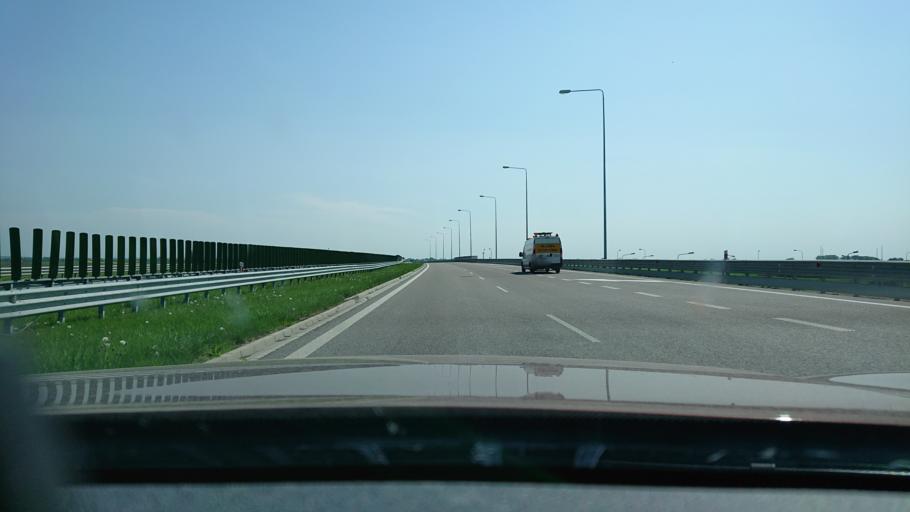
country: PL
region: Subcarpathian Voivodeship
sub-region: Powiat jaroslawski
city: Radymno
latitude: 49.9105
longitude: 22.8157
